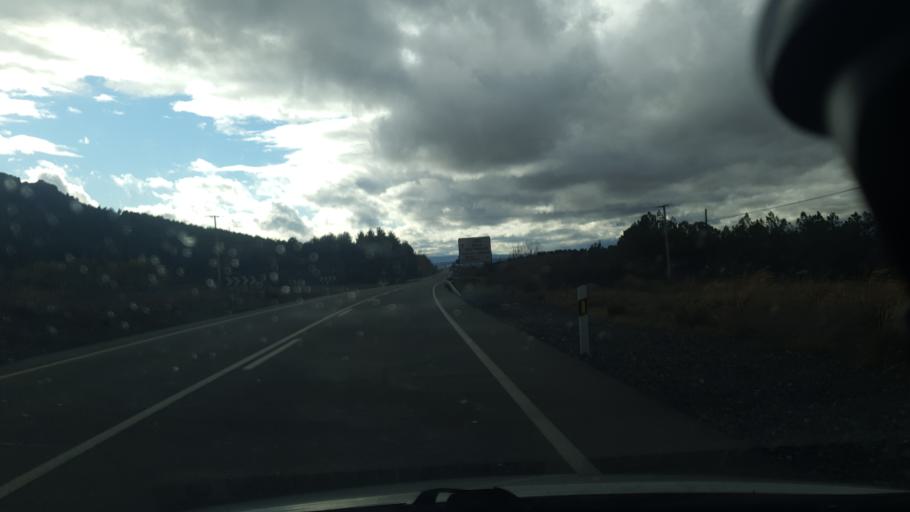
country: ES
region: Castille and Leon
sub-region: Provincia de Avila
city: Ojos-Albos
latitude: 40.7363
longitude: -4.4903
